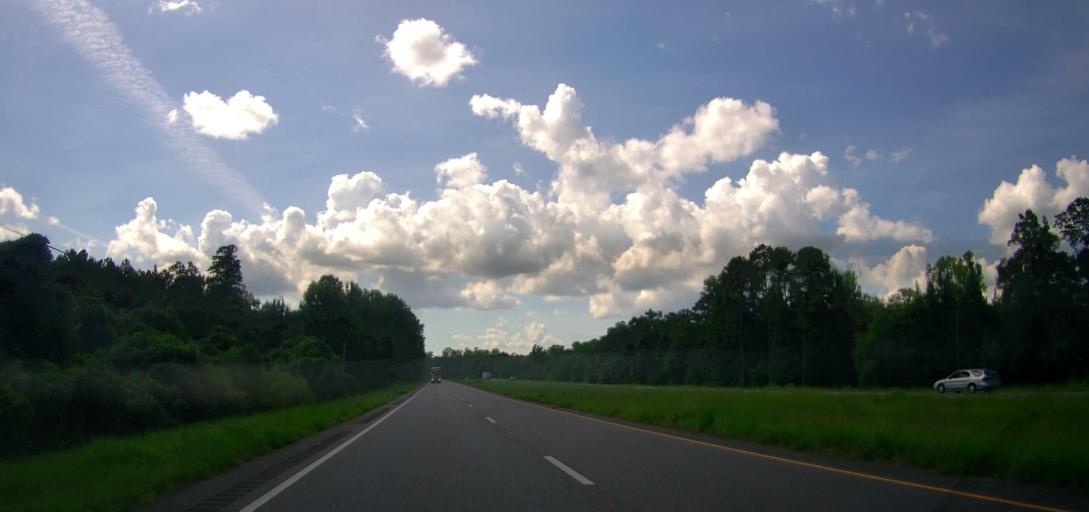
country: US
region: Alabama
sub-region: Pickens County
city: Reform
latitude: 33.3676
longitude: -87.9844
